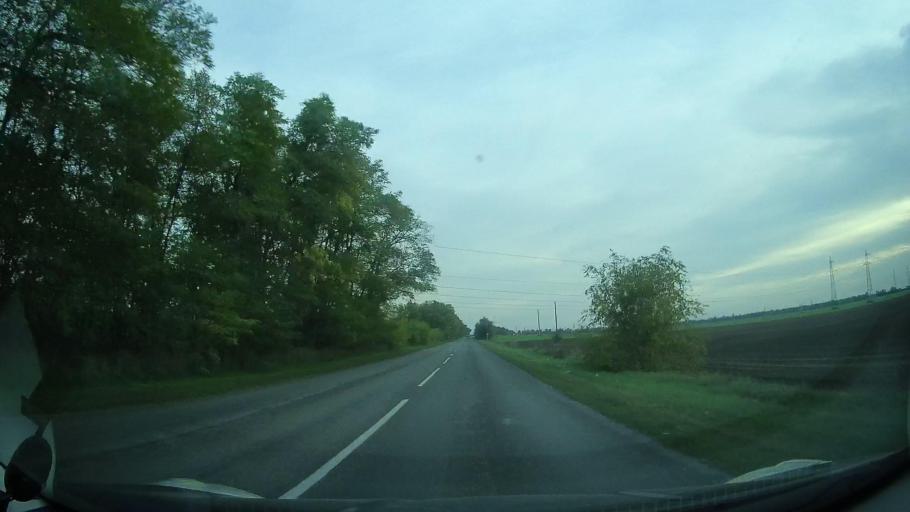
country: RU
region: Rostov
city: Ol'ginskaya
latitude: 47.1119
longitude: 39.9773
